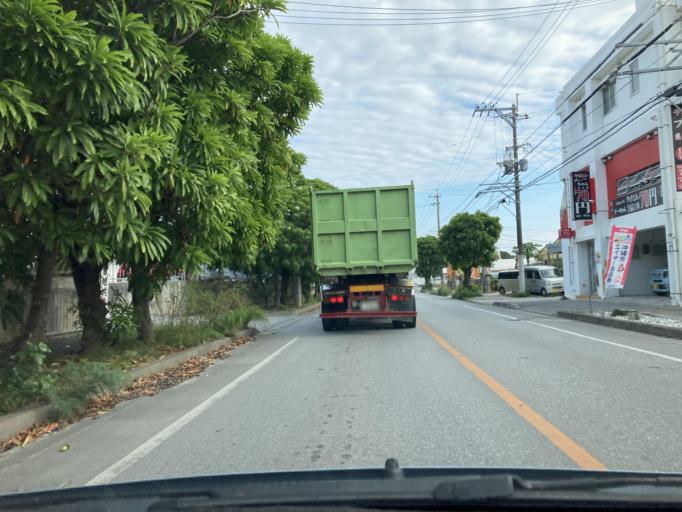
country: JP
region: Okinawa
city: Okinawa
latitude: 26.3682
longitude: 127.8158
